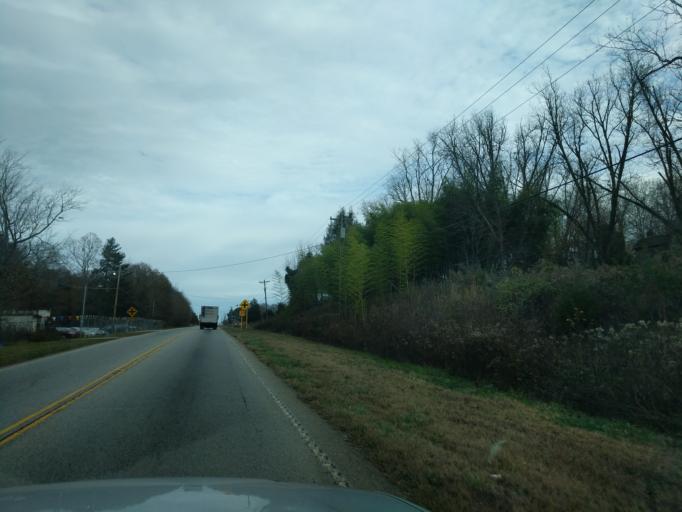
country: US
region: South Carolina
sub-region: Anderson County
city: Williamston
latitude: 34.6412
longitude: -82.4444
